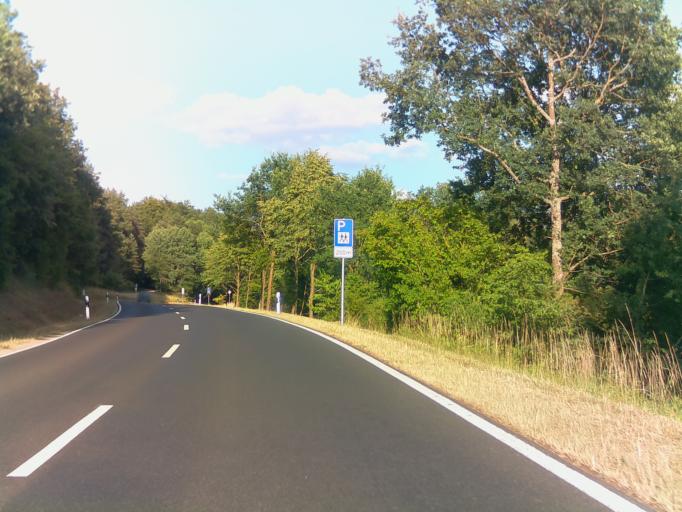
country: DE
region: Bavaria
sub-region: Regierungsbezirk Unterfranken
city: Oberelsbach
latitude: 50.4243
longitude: 10.1457
